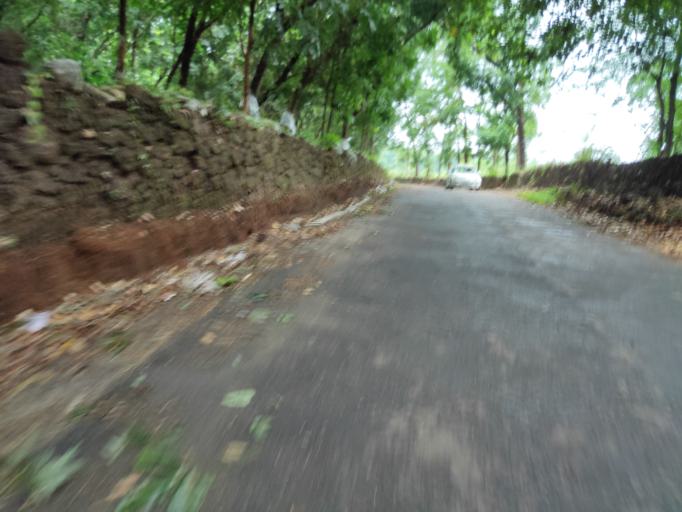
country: IN
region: Kerala
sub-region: Malappuram
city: Manjeri
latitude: 11.2333
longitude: 76.2500
